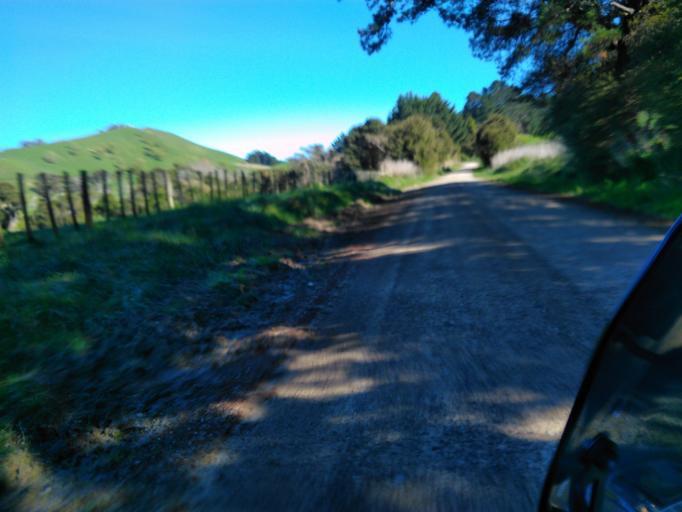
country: NZ
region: Gisborne
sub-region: Gisborne District
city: Gisborne
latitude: -38.4237
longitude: 177.7094
